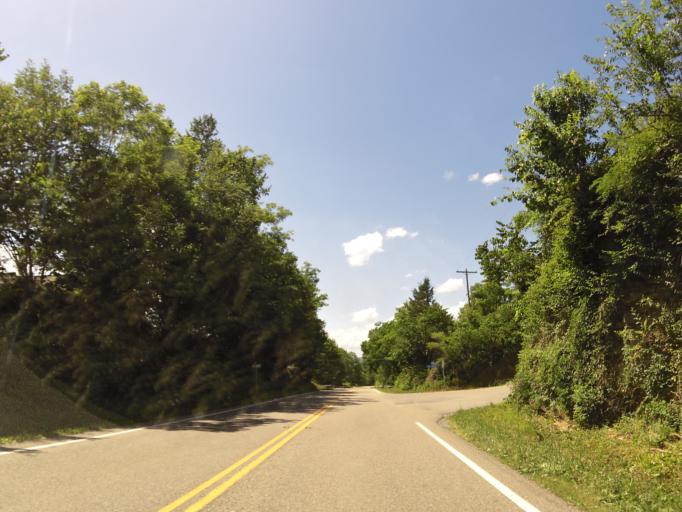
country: US
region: Virginia
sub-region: Lee County
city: Pennington Gap
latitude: 36.7186
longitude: -82.9800
